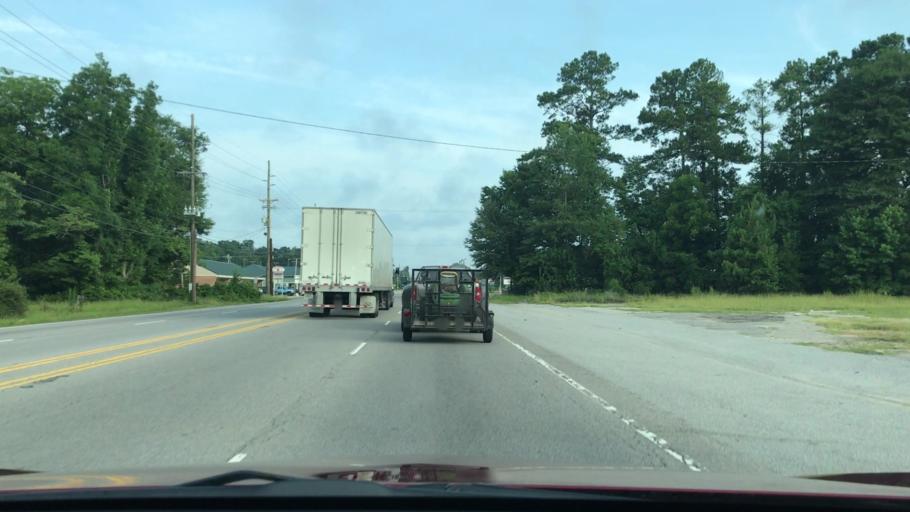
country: US
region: South Carolina
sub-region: Orangeburg County
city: Wilkinson Heights
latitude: 33.4793
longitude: -80.8201
